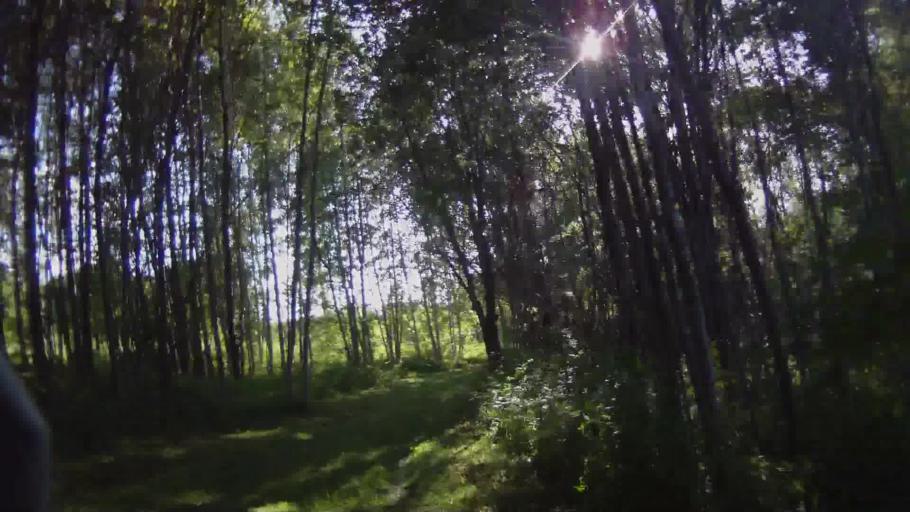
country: LV
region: Dagda
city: Dagda
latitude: 56.2753
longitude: 27.4707
